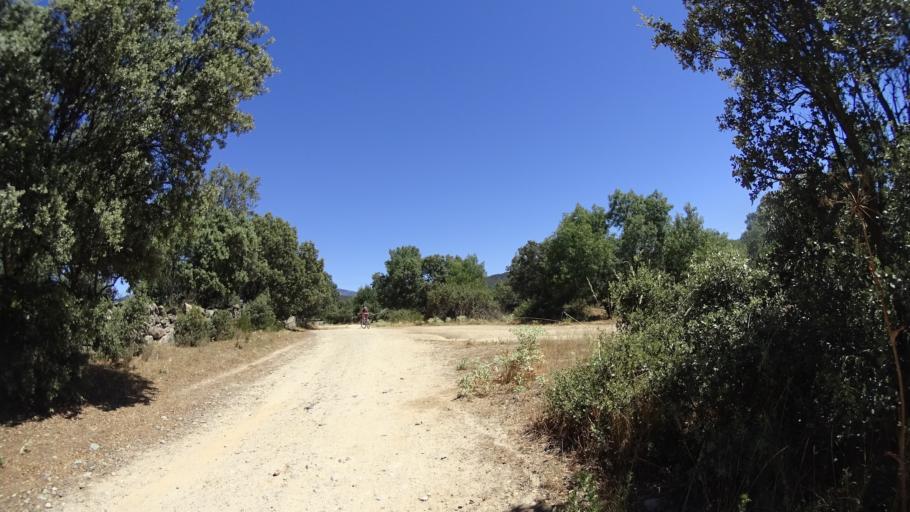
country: ES
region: Madrid
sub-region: Provincia de Madrid
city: Alpedrete
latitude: 40.6750
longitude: -4.0387
